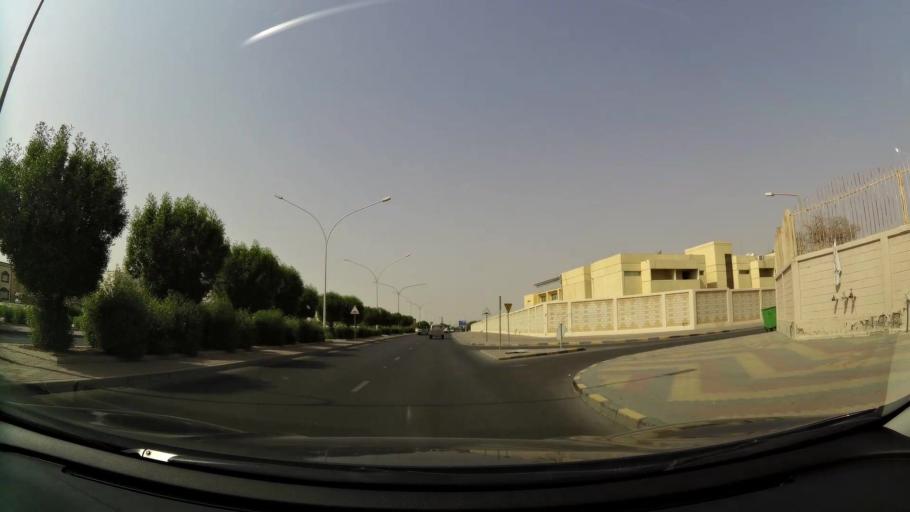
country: KW
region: Muhafazat al Jahra'
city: Al Jahra'
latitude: 29.3370
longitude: 47.6953
